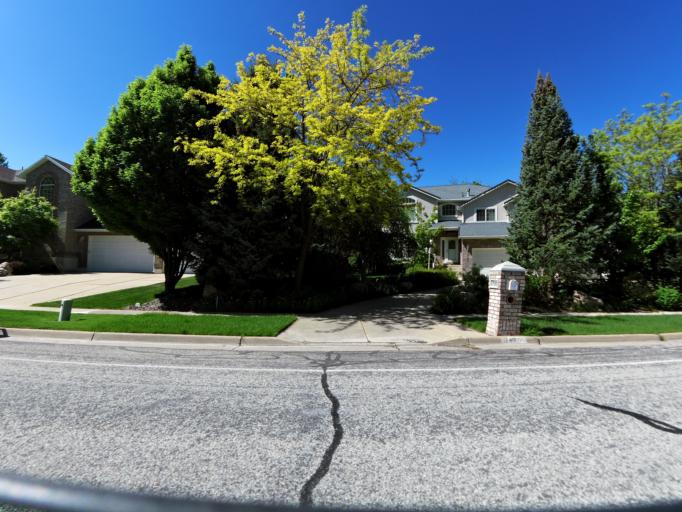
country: US
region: Utah
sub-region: Weber County
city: Uintah
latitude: 41.1675
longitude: -111.9323
